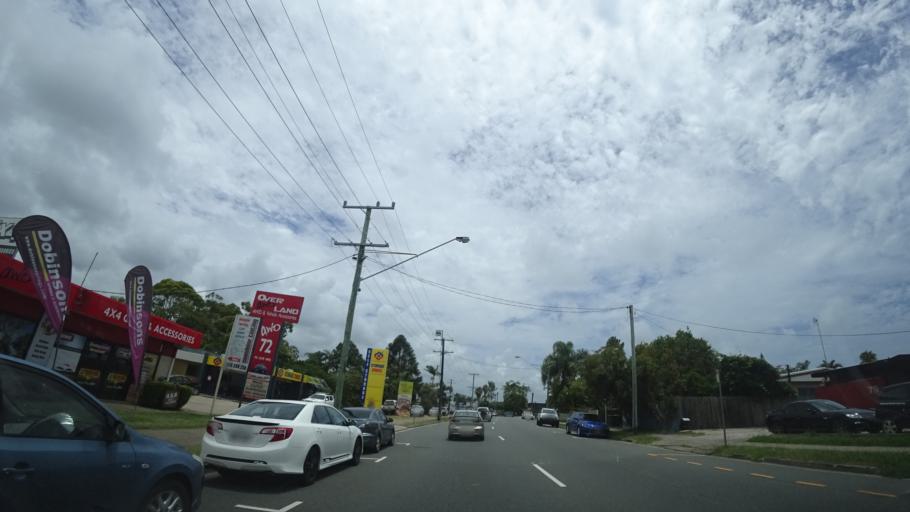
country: AU
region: Queensland
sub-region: Sunshine Coast
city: Mooloolaba
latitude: -26.6682
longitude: 153.0940
